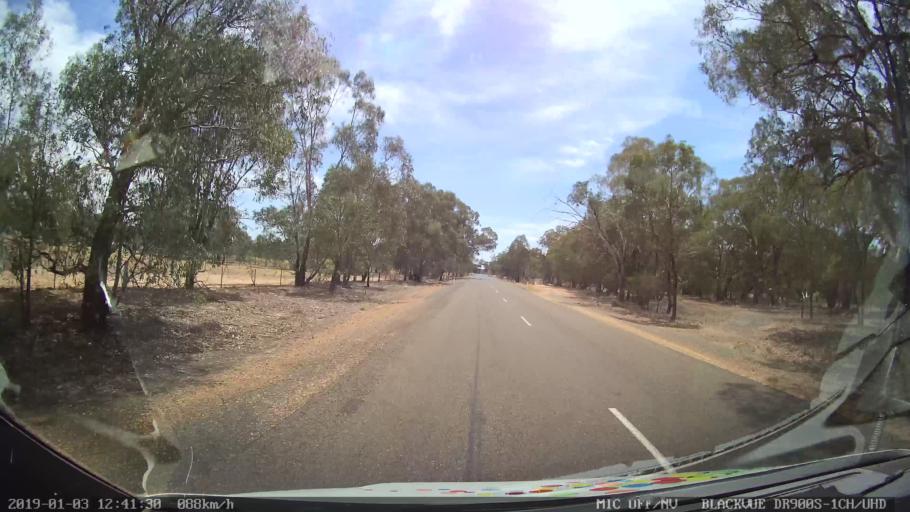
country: AU
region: New South Wales
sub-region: Weddin
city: Grenfell
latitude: -33.7988
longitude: 148.2151
